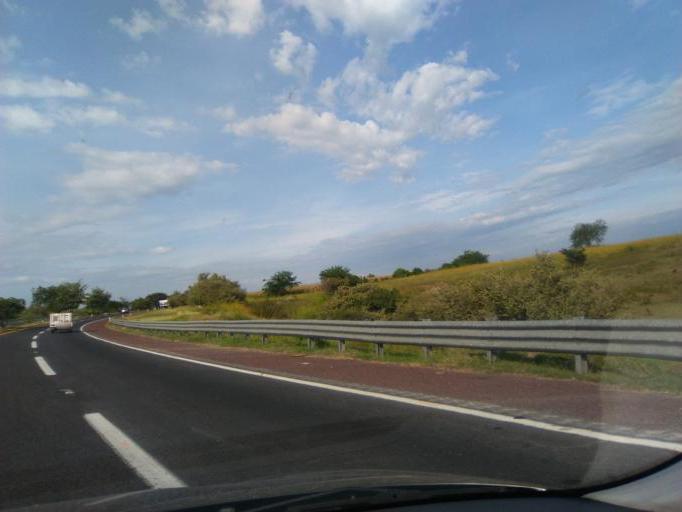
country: MX
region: Morelos
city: Ahuehuetzingo
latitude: 18.6721
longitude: -99.2946
